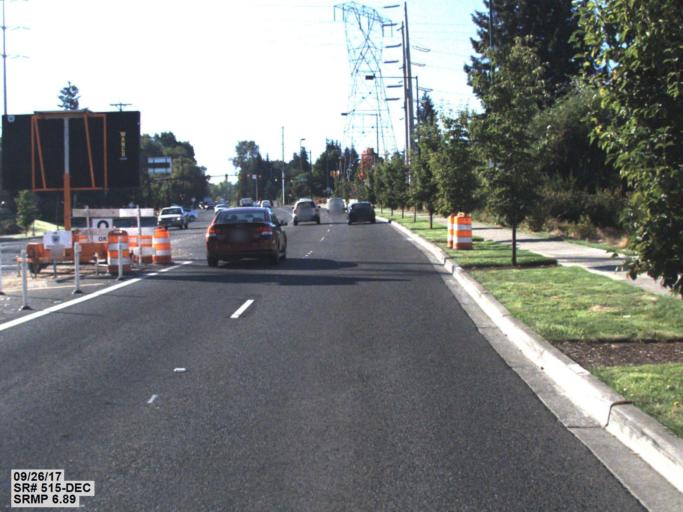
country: US
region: Washington
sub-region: King County
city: Renton
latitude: 47.4685
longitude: -122.2080
